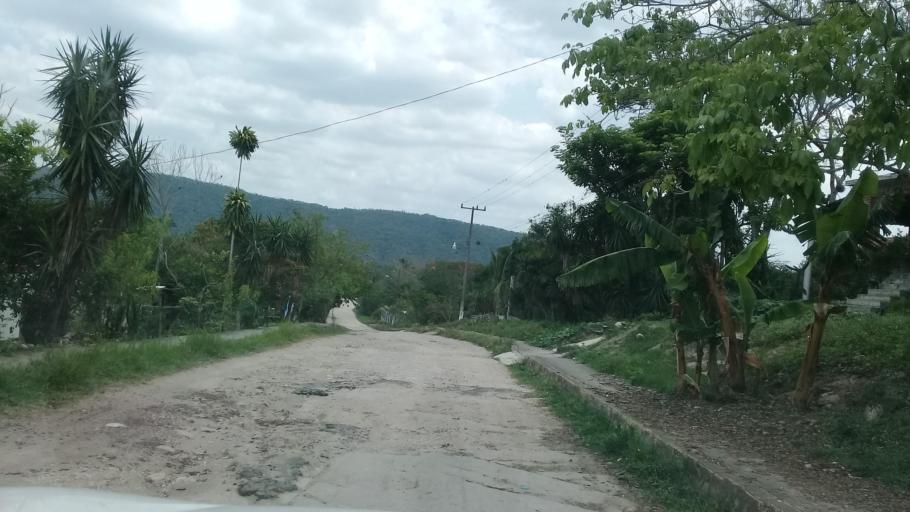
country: MX
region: Veracruz
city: Jalcomulco
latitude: 19.3885
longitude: -96.7933
